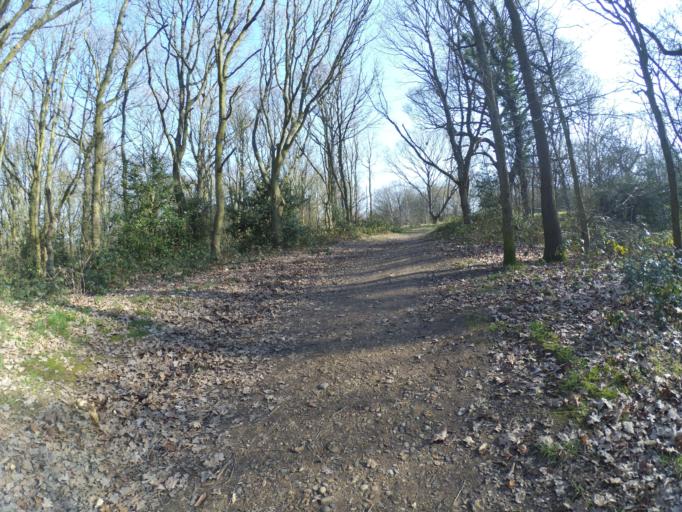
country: GB
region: England
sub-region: Greater London
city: Wembley
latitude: 51.5741
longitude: -0.2815
